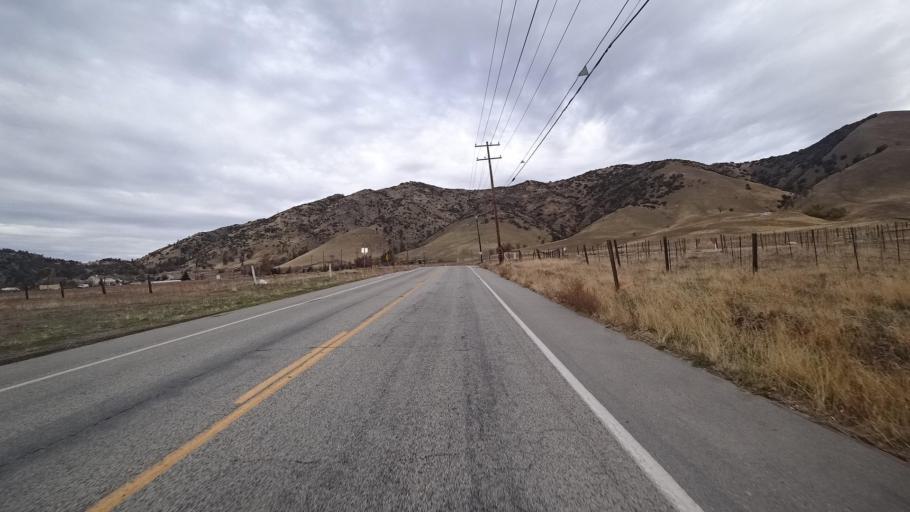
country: US
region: California
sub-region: Kern County
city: Bear Valley Springs
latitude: 35.1442
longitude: -118.5756
